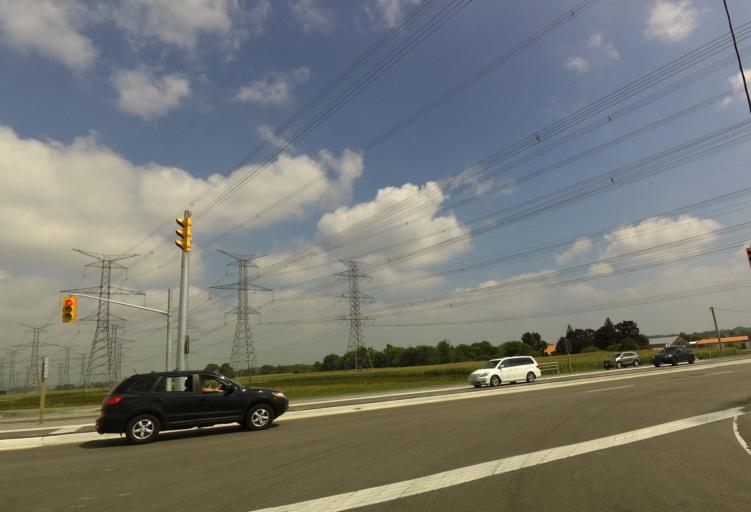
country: CA
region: Ontario
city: Oshawa
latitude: 43.9493
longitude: -78.9403
